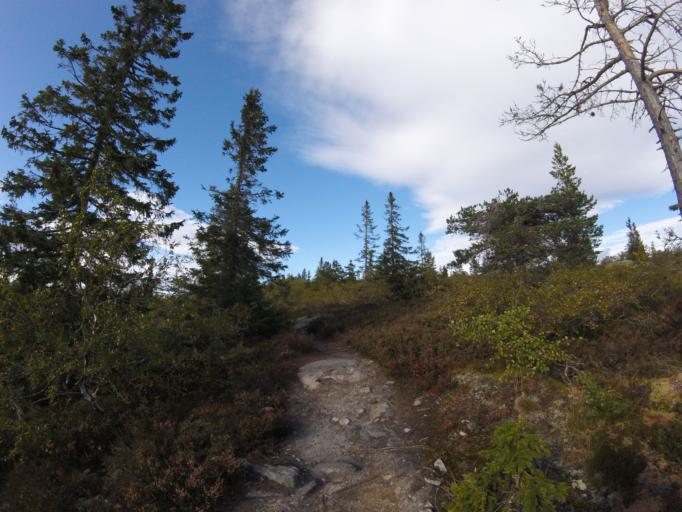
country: NO
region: Buskerud
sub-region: Flesberg
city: Lampeland
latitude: 59.7672
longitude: 9.4119
